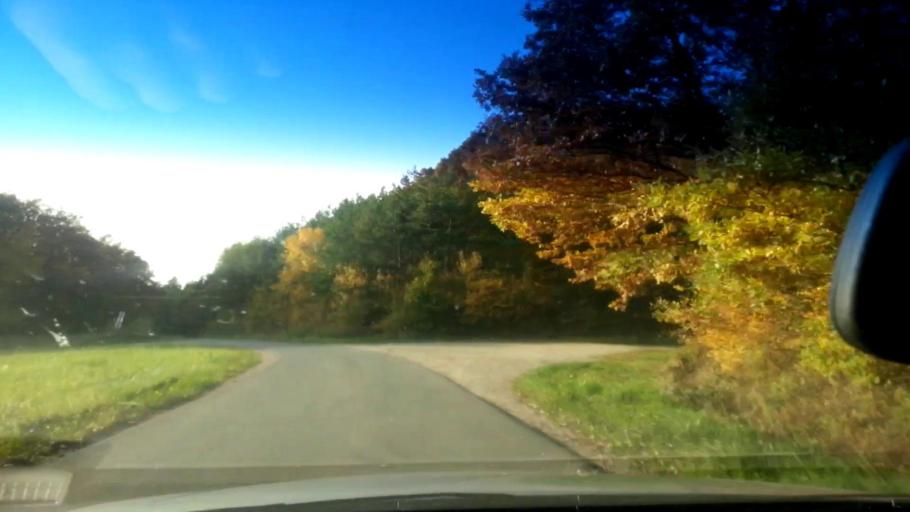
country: DE
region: Bavaria
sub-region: Upper Franconia
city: Schesslitz
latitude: 50.0189
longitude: 11.0208
